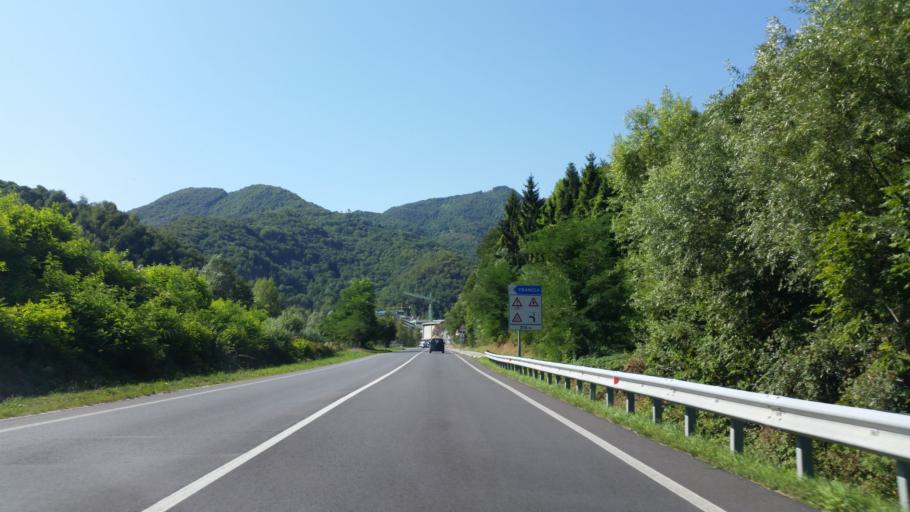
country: IT
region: Piedmont
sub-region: Provincia di Cuneo
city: Robilante
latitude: 44.2665
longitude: 7.5185
